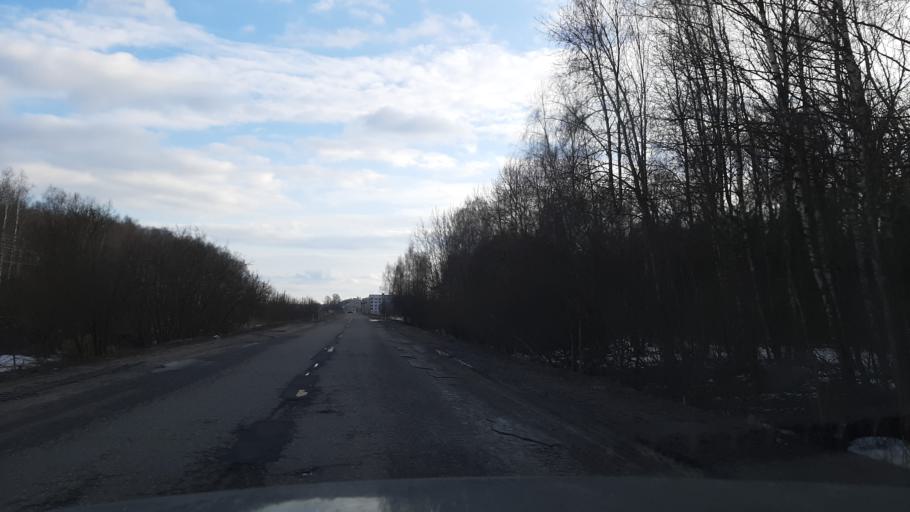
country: RU
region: Ivanovo
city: Novo-Talitsy
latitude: 56.9306
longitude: 40.7351
